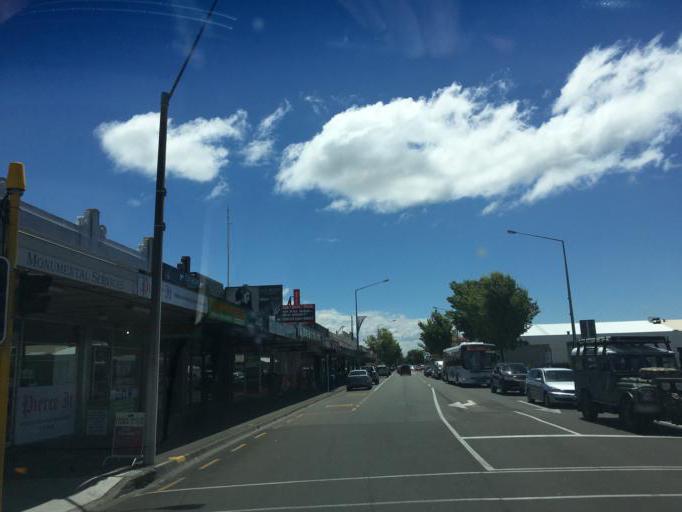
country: NZ
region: Hawke's Bay
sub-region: Hastings District
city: Hastings
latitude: -39.6390
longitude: 176.8401
